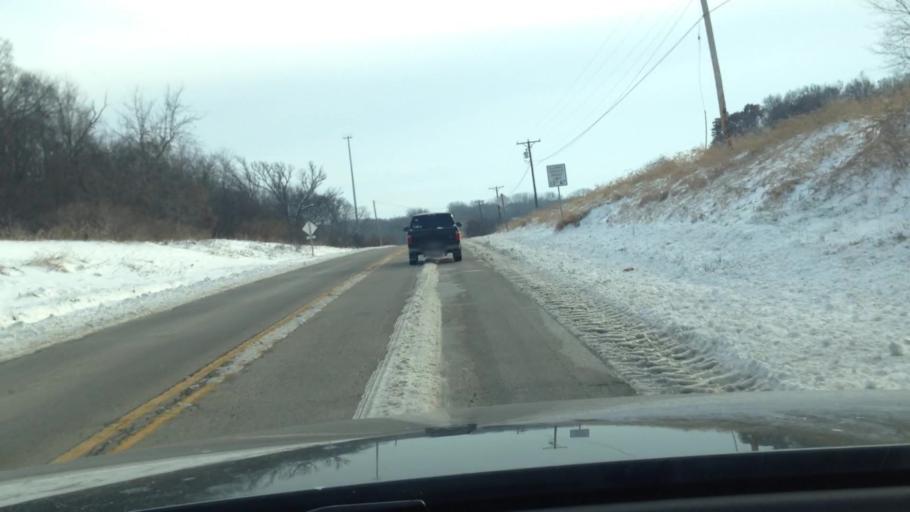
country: US
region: Illinois
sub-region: McHenry County
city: Hebron
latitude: 42.4925
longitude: -88.4424
